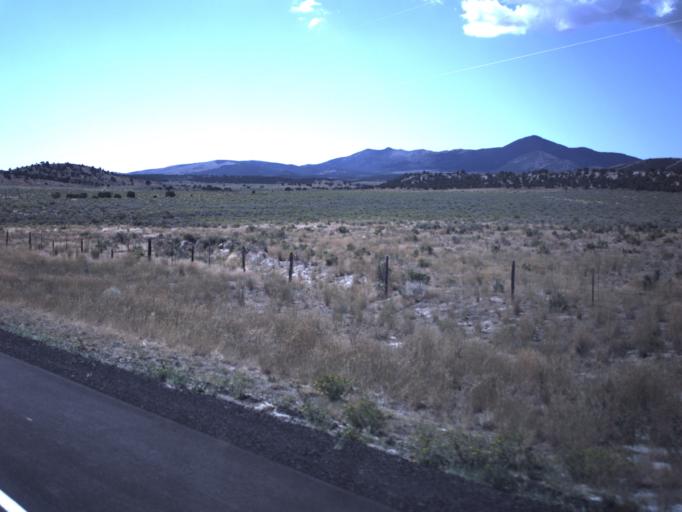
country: US
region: Utah
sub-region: Utah County
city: Eagle Mountain
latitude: 40.0492
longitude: -112.2952
